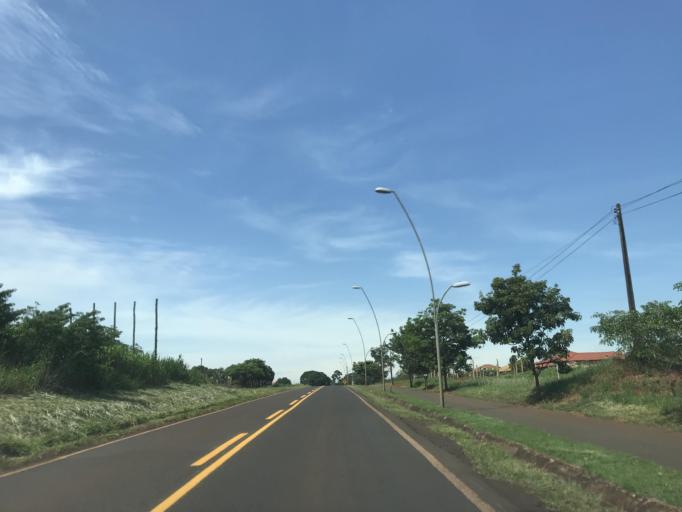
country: BR
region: Parana
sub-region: Terra Rica
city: Terra Rica
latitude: -22.7476
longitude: -52.6252
